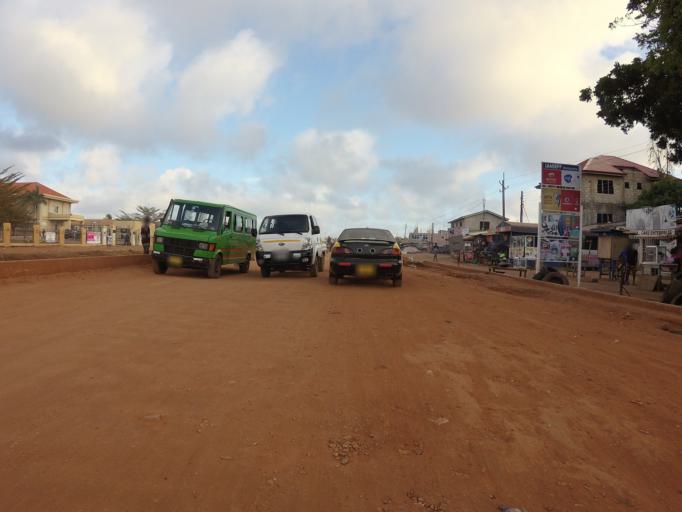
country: GH
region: Greater Accra
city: Teshi Old Town
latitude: 5.6029
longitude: -0.1210
